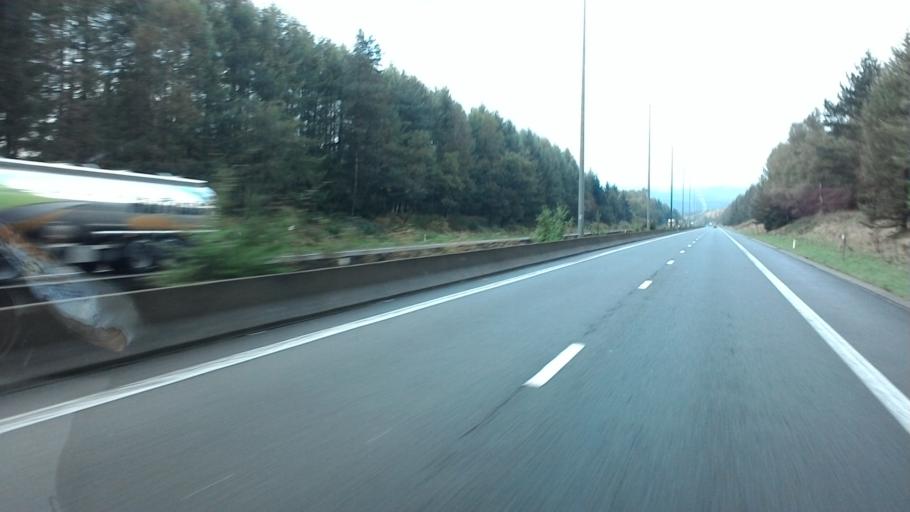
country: BE
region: Wallonia
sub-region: Province du Luxembourg
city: Manhay
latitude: 50.2695
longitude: 5.7267
